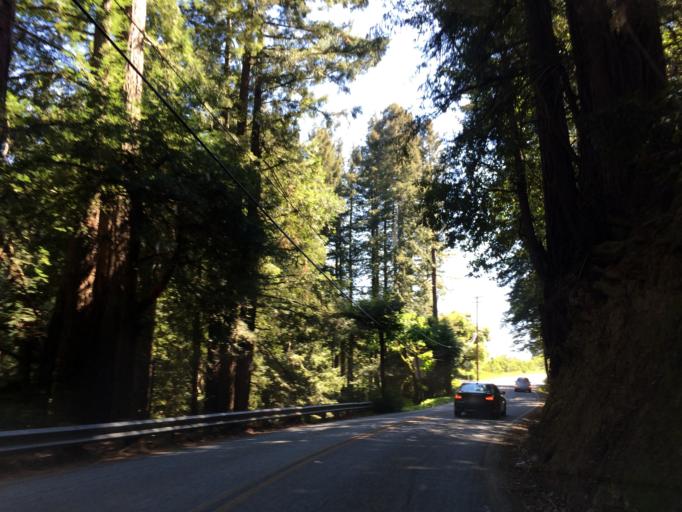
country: US
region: California
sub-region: Santa Clara County
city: Lexington Hills
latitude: 37.1668
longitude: -122.0166
